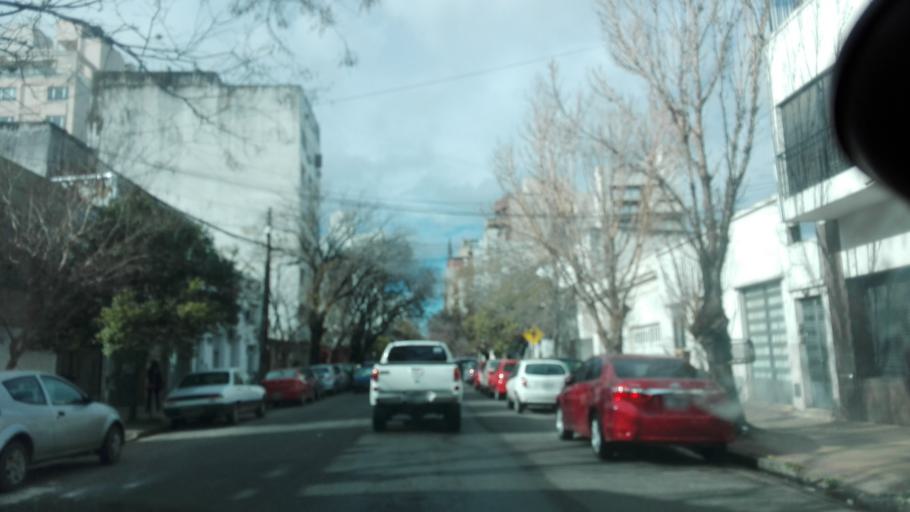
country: AR
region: Buenos Aires
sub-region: Partido de La Plata
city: La Plata
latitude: -34.9183
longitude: -57.9612
